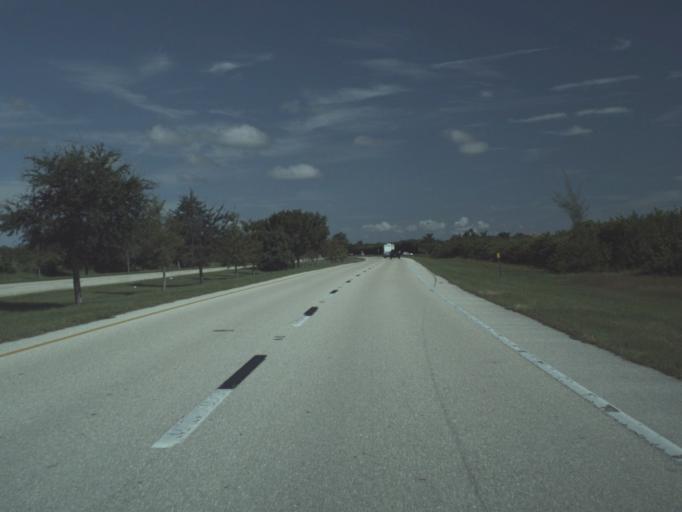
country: US
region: Florida
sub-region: Lee County
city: Pine Island Center
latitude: 26.6211
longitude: -82.0407
